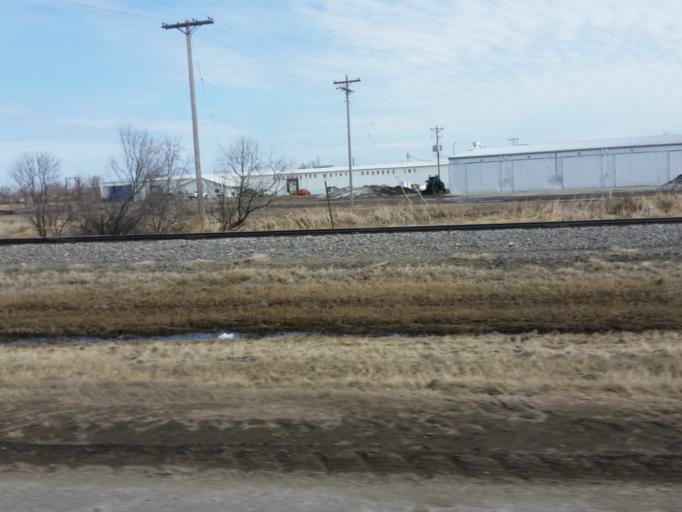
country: US
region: North Dakota
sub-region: Walsh County
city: Grafton
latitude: 48.4055
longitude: -97.4056
